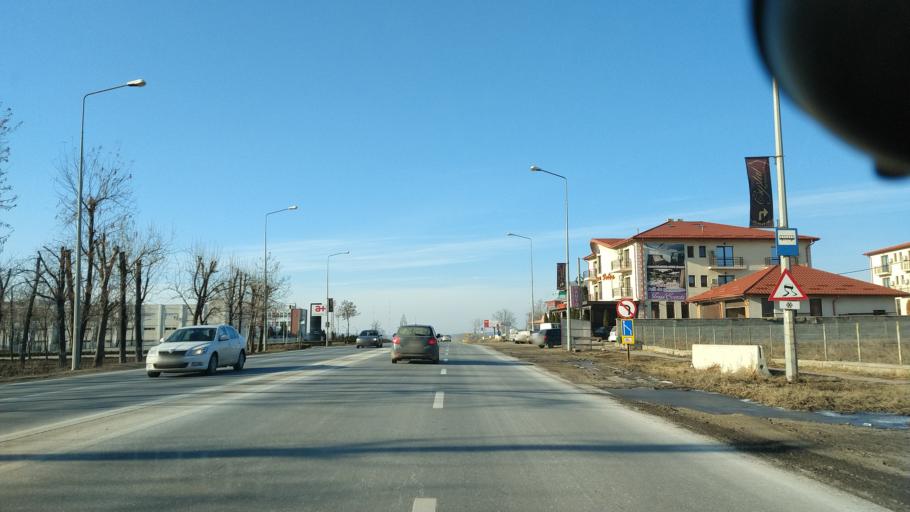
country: RO
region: Iasi
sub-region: Comuna Valea Lupului
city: Valea Lupului
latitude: 47.1772
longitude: 27.4895
